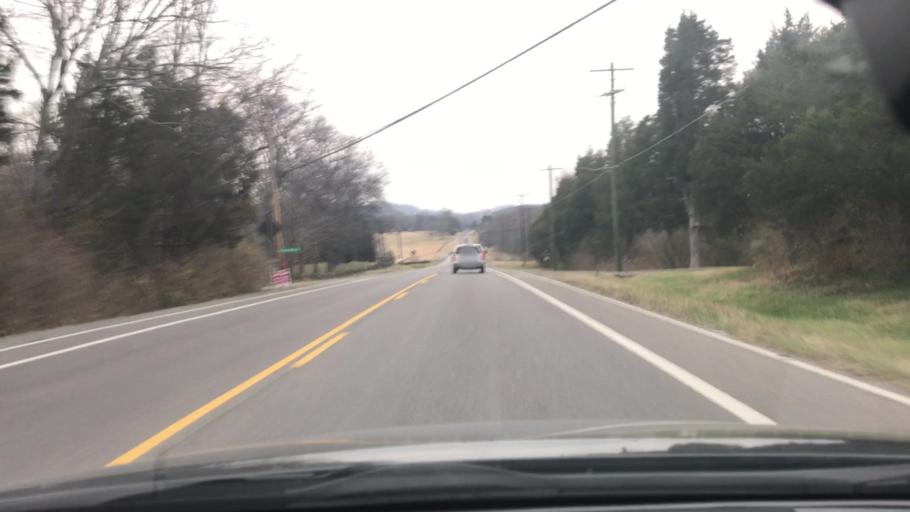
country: US
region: Tennessee
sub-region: Davidson County
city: Forest Hills
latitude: 36.0343
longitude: -86.8737
